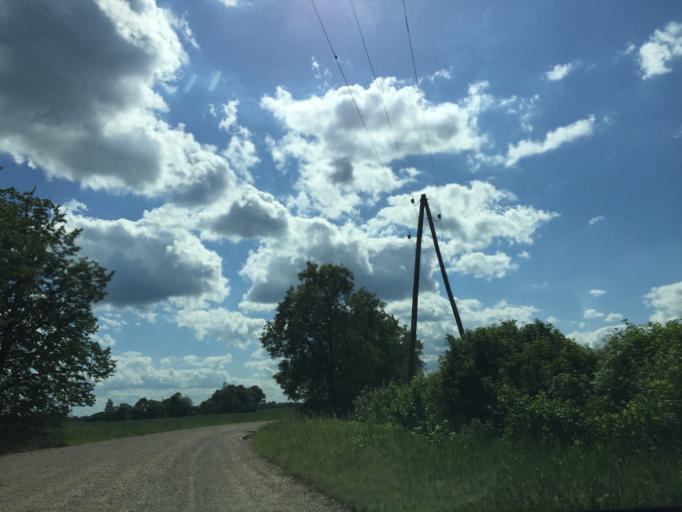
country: LV
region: Engure
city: Smarde
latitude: 56.8597
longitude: 23.3169
